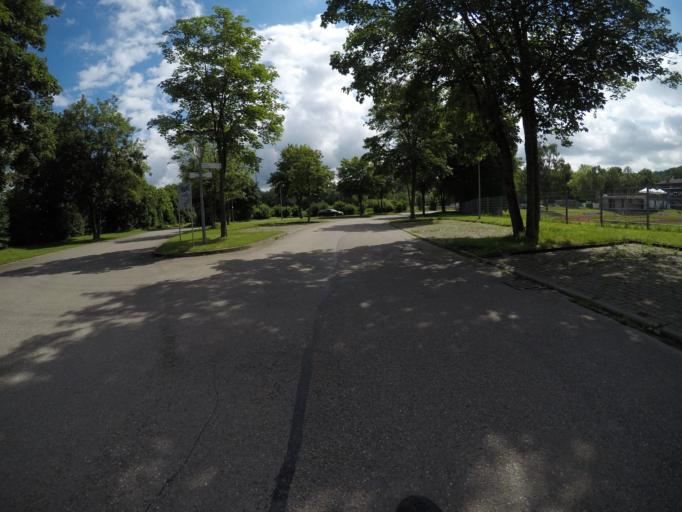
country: DE
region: Baden-Wuerttemberg
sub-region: Regierungsbezirk Stuttgart
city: Reichenbach an der Fils
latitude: 48.7066
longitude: 9.4771
